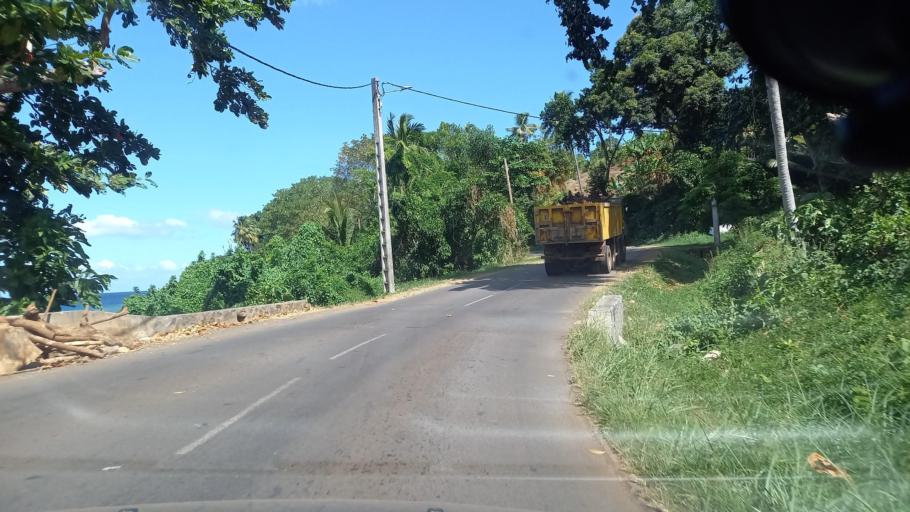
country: YT
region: M'Tsangamouji
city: M'Tsangamouji
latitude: -12.7647
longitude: 45.0801
